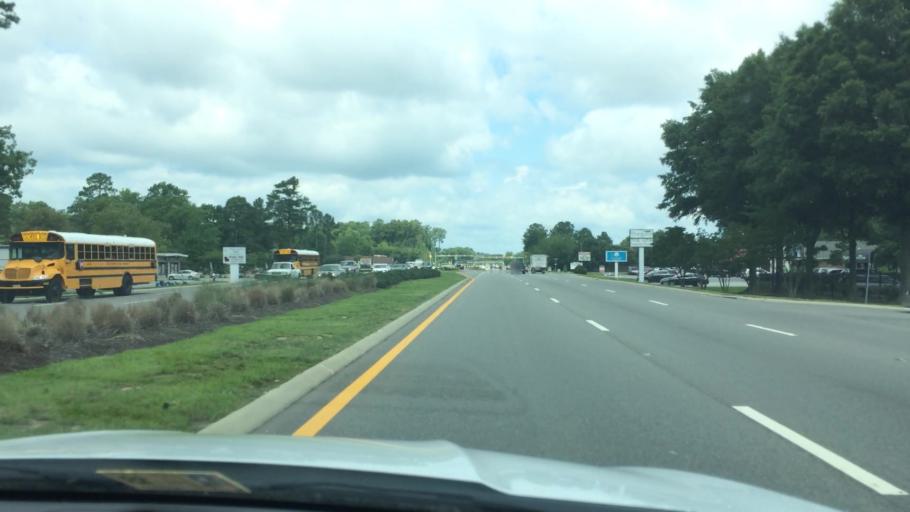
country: US
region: Virginia
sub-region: York County
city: Yorktown
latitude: 37.1520
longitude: -76.4605
